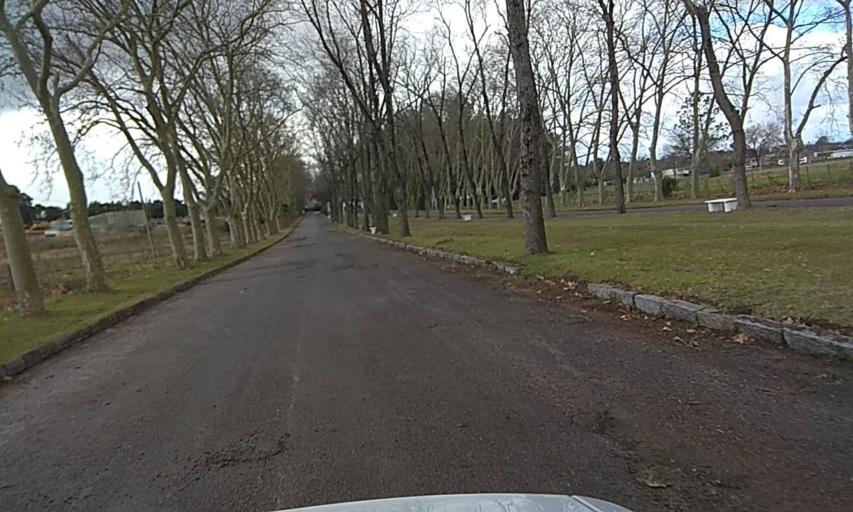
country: UY
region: Florida
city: Florida
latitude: -34.1073
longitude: -56.2272
